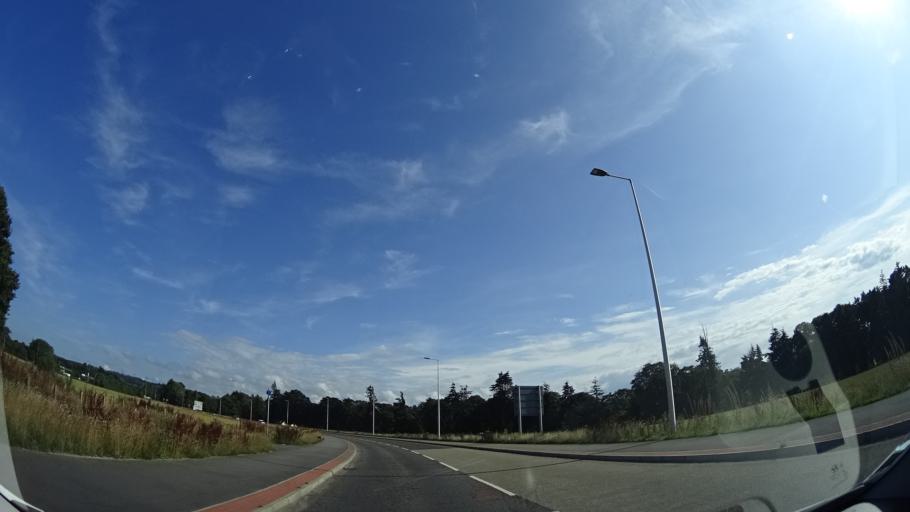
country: GB
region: Scotland
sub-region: Highland
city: Inverness
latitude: 57.4521
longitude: -4.2562
